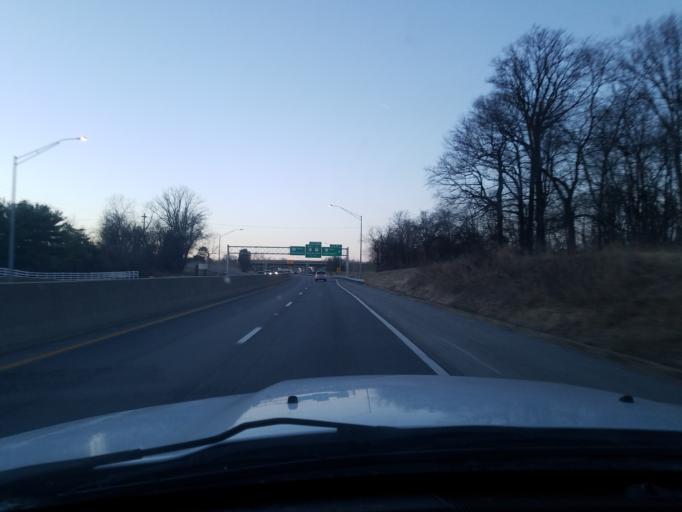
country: US
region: Kentucky
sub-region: Henderson County
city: Henderson
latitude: 37.8539
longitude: -87.5699
